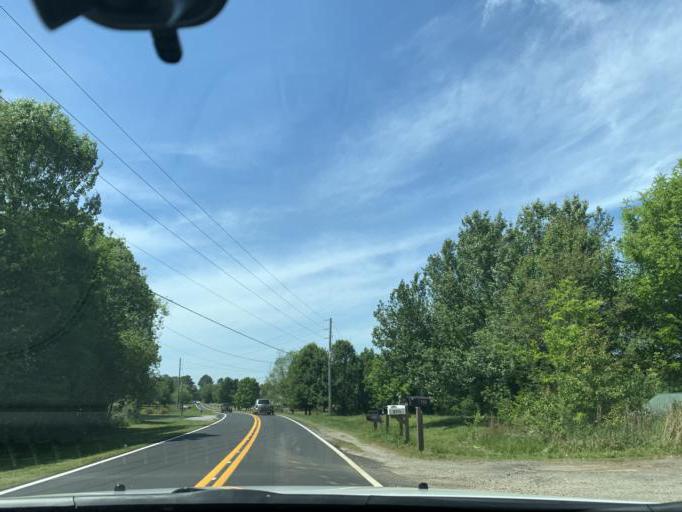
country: US
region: Georgia
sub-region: Forsyth County
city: Cumming
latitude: 34.2593
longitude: -84.0286
